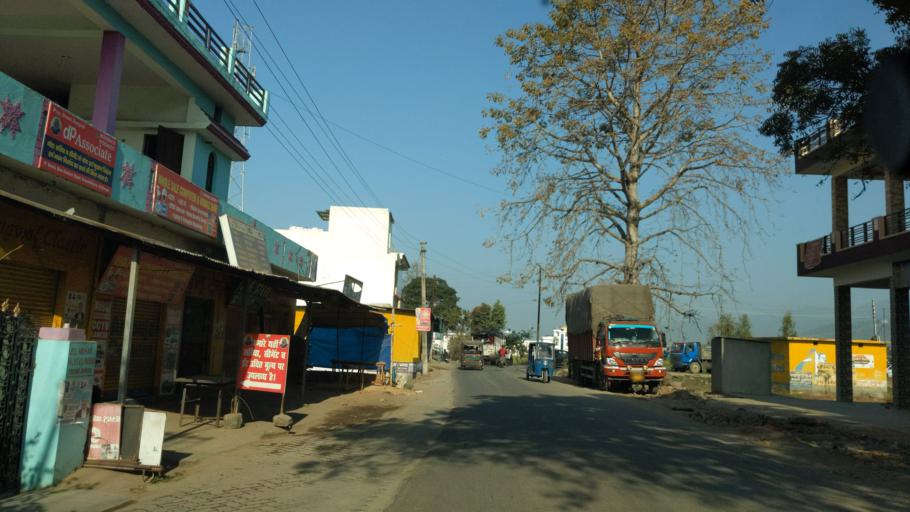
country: IN
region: Uttarakhand
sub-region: Naini Tal
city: Haldwani
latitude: 29.2083
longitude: 79.4943
